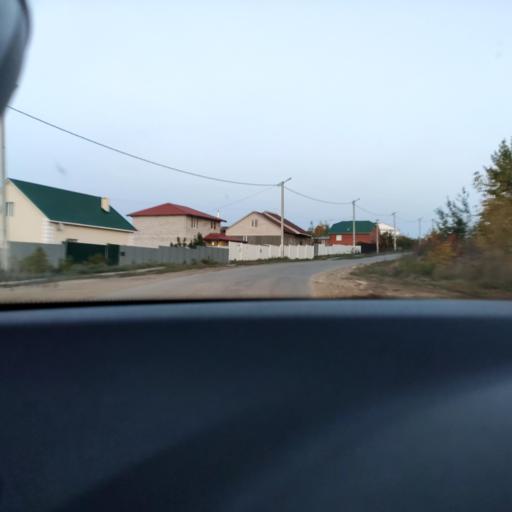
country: RU
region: Samara
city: Novosemeykino
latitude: 53.3828
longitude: 50.3203
